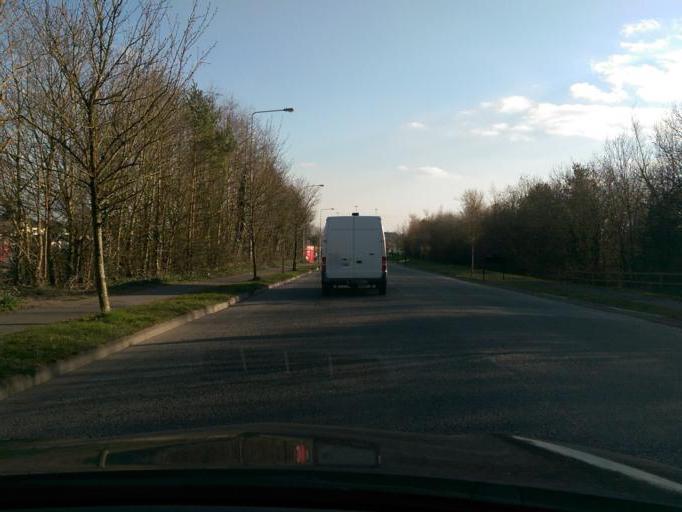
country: IE
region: Leinster
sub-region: Kildare
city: Kildare
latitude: 53.1568
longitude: -6.9194
